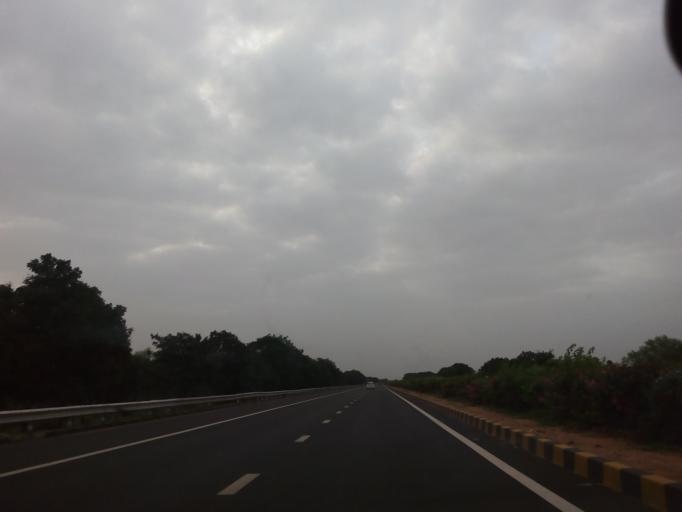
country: IN
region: Gujarat
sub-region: Kheda
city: Mahemdavad
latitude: 22.9229
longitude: 72.7484
